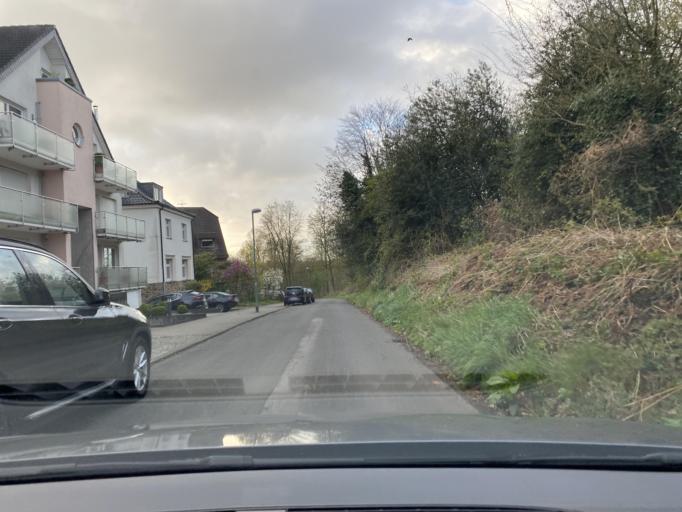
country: DE
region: North Rhine-Westphalia
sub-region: Regierungsbezirk Dusseldorf
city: Essen
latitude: 51.4074
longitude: 6.9891
